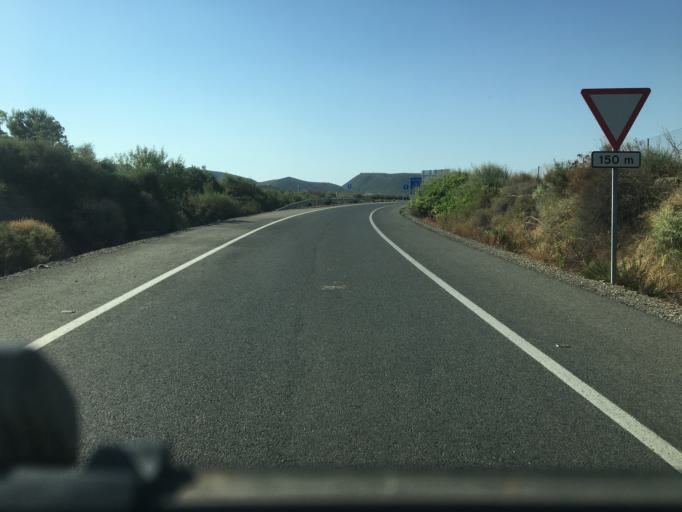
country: ES
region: Murcia
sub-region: Murcia
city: Puerto Lumbreras
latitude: 37.5371
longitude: -1.8160
